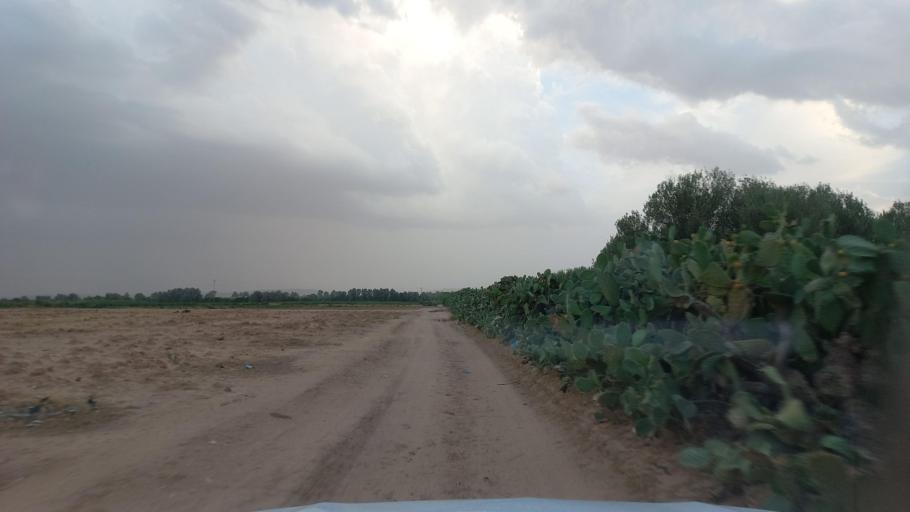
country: TN
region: Al Qasrayn
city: Kasserine
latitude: 35.2771
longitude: 9.0591
